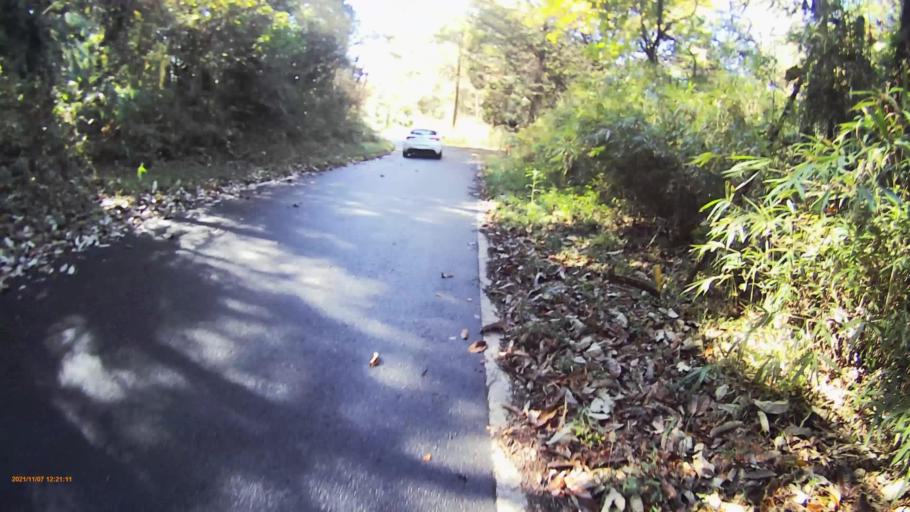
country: JP
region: Gifu
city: Mizunami
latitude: 35.4397
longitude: 137.2659
